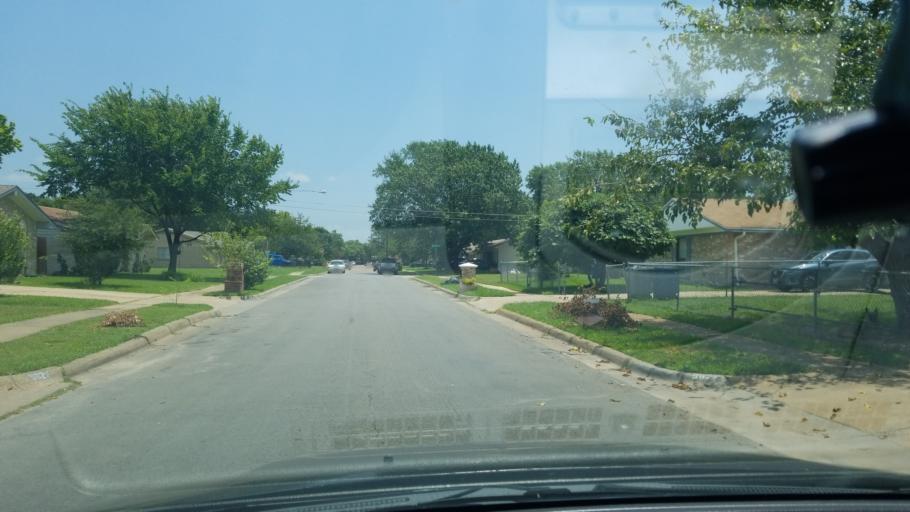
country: US
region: Texas
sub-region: Dallas County
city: Balch Springs
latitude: 32.7140
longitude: -96.6534
